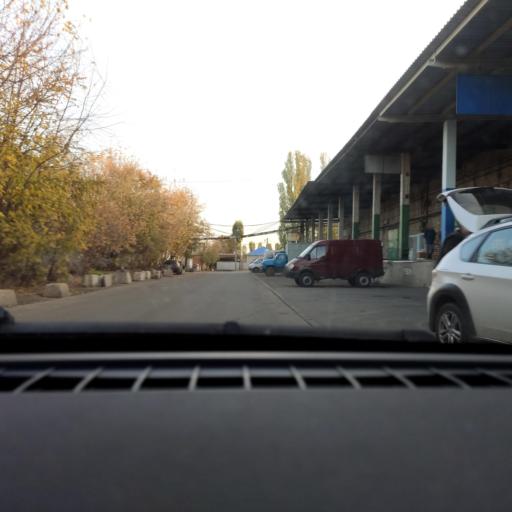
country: RU
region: Voronezj
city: Voronezh
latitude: 51.6564
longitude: 39.2702
